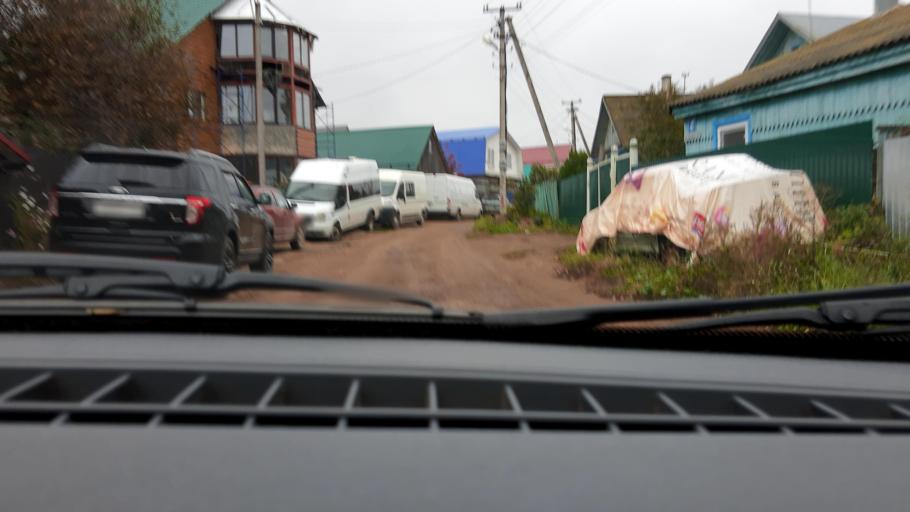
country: RU
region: Bashkortostan
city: Mikhaylovka
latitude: 54.7957
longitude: 55.8822
